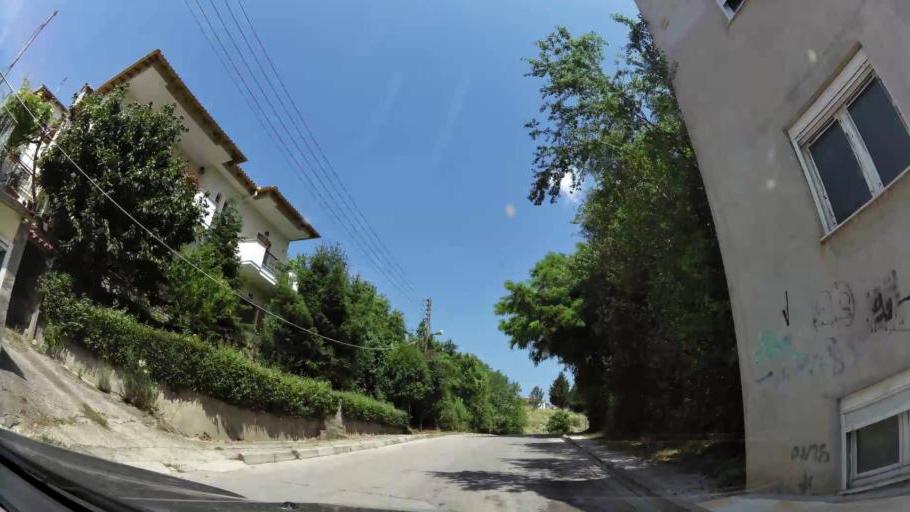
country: GR
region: West Macedonia
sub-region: Nomos Kozanis
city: Kozani
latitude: 40.3012
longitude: 21.7803
